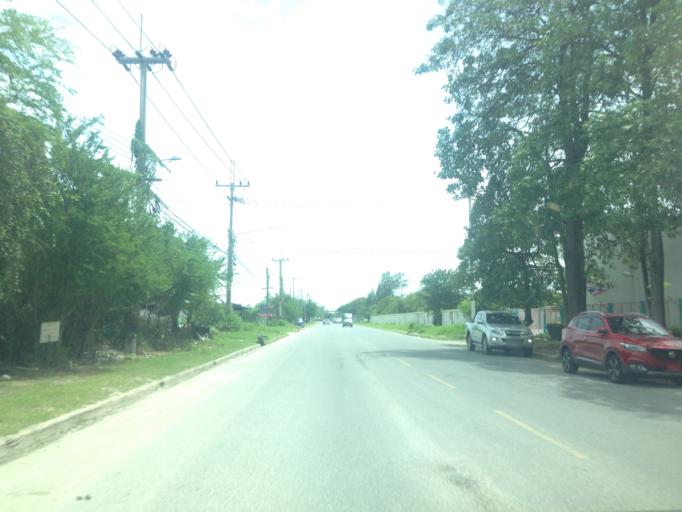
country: TH
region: Chon Buri
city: Chon Buri
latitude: 13.3439
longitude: 100.9529
